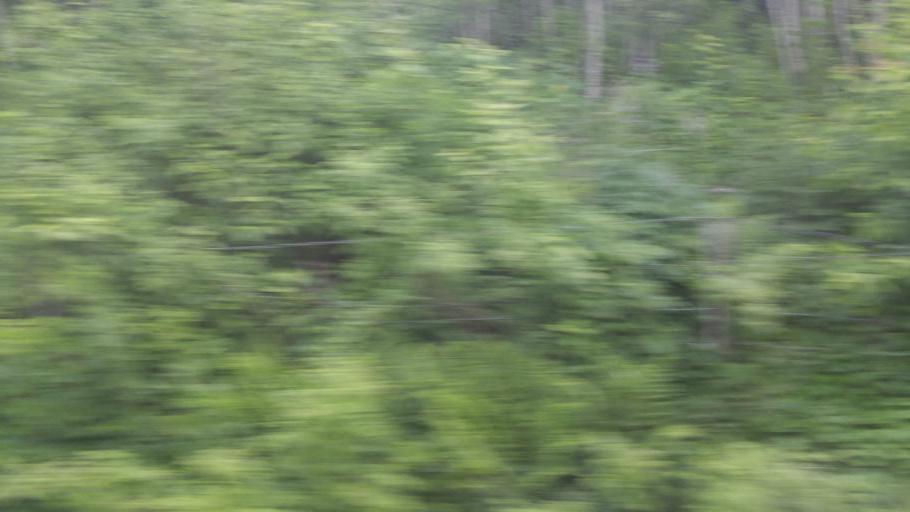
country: NO
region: Sor-Trondelag
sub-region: Melhus
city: Lundamo
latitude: 63.2144
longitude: 10.3116
